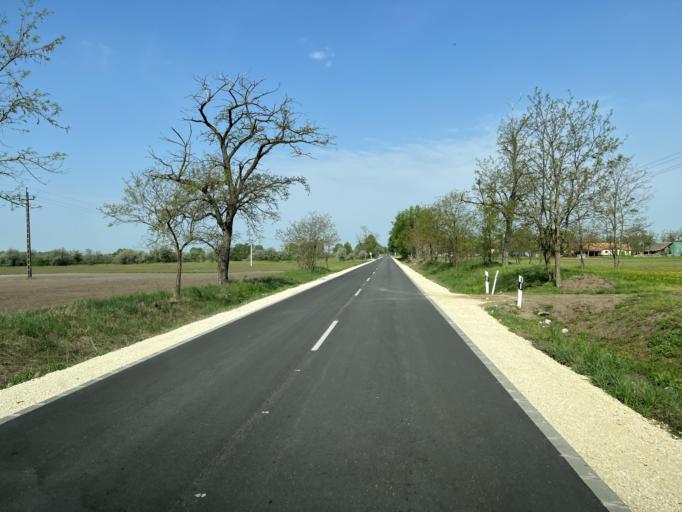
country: HU
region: Pest
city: Kocser
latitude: 46.9949
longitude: 19.9484
